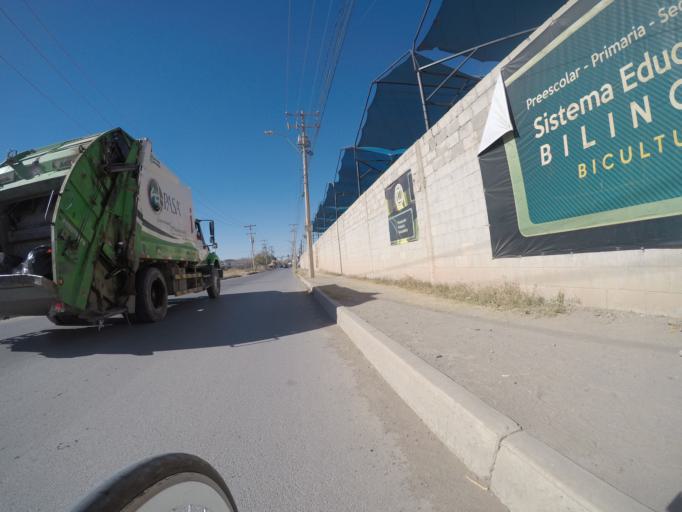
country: MX
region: Chihuahua
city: Ciudad Juarez
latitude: 31.6960
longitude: -106.4023
